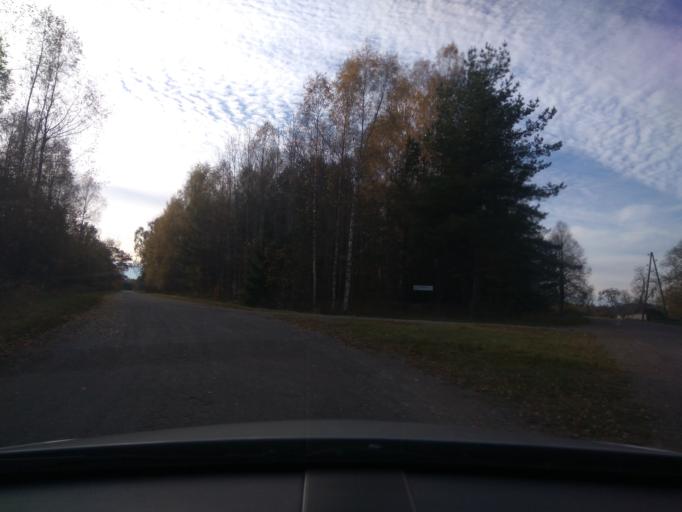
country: LV
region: Kuldigas Rajons
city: Kuldiga
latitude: 56.9176
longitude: 21.9003
